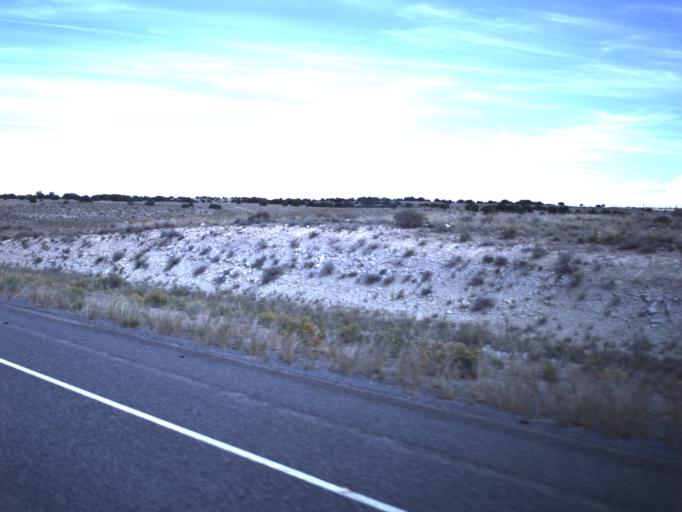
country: US
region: Utah
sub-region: Emery County
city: Castle Dale
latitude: 38.8845
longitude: -110.6533
